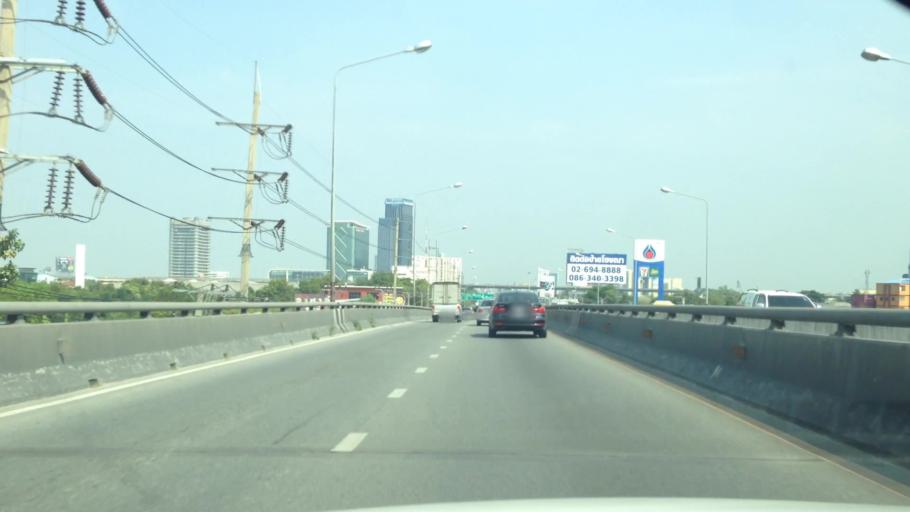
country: TH
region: Bangkok
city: Bang Na
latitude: 13.6565
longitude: 100.6422
